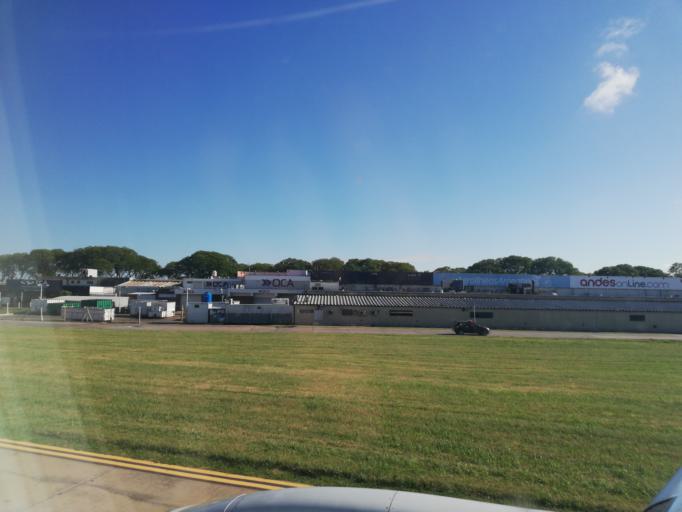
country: AR
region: Buenos Aires F.D.
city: Colegiales
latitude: -34.5555
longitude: -58.4208
